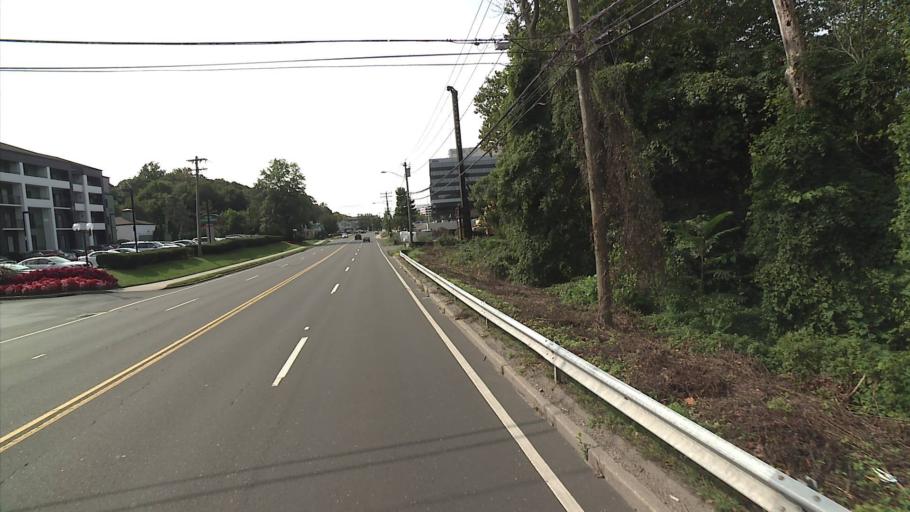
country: US
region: Connecticut
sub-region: Fairfield County
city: Norwalk
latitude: 41.1531
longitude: -73.4246
